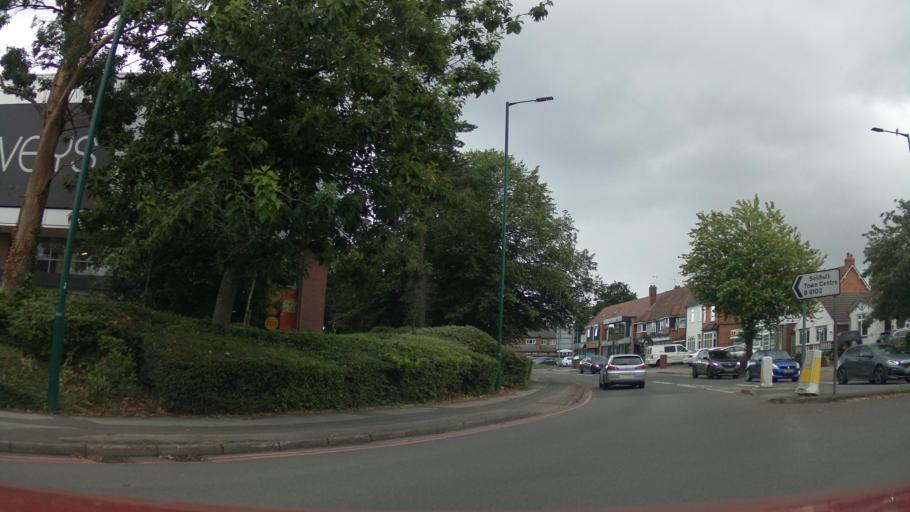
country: GB
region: England
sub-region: Solihull
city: Shirley
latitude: 52.3995
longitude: -1.8161
